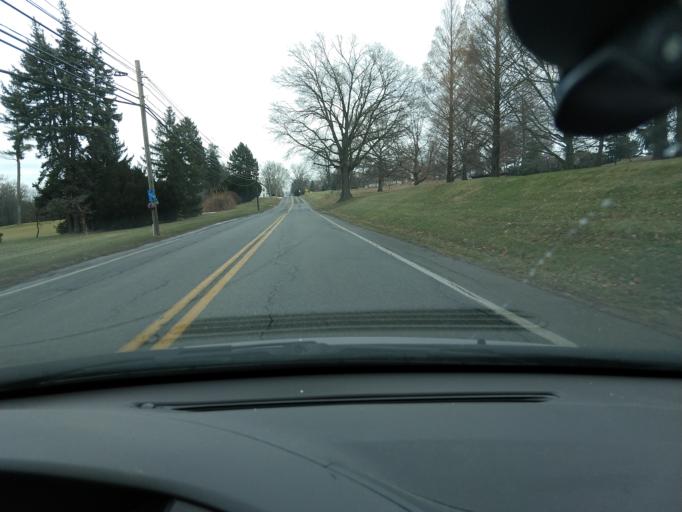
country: US
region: Pennsylvania
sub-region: Chester County
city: South Pottstown
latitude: 40.2329
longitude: -75.6439
